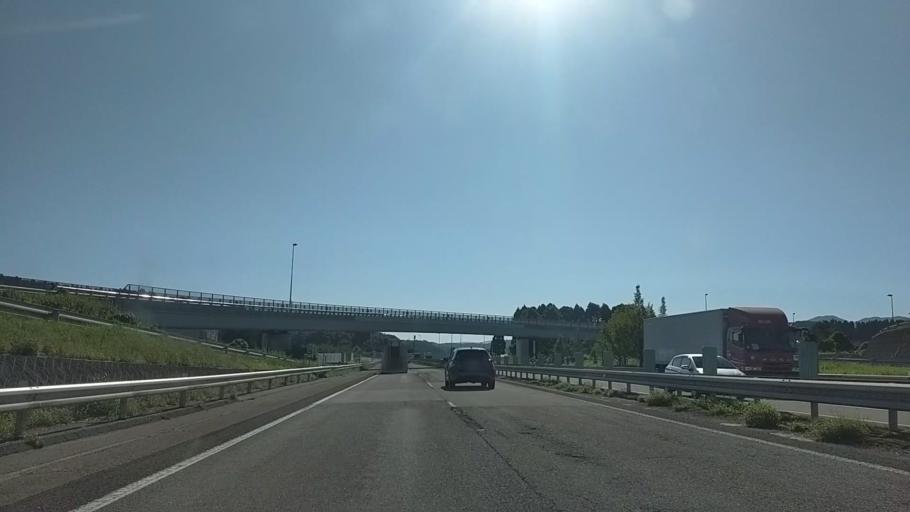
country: JP
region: Ishikawa
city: Tsubata
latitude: 36.6072
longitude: 136.7055
